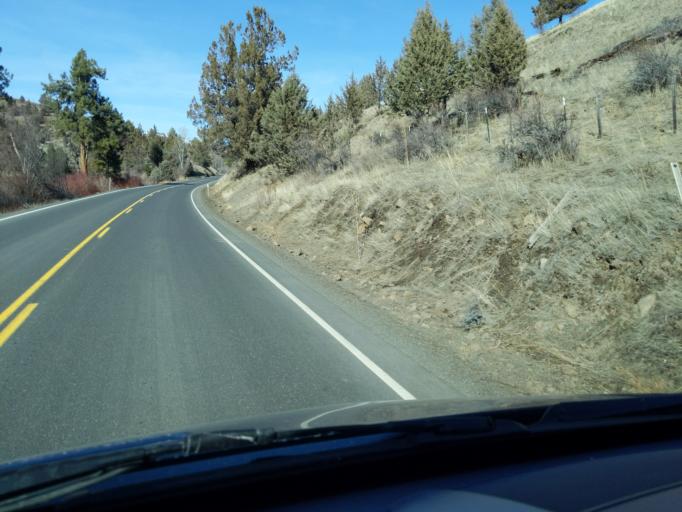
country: US
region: Oregon
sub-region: Grant County
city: John Day
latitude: 44.8444
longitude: -119.0319
